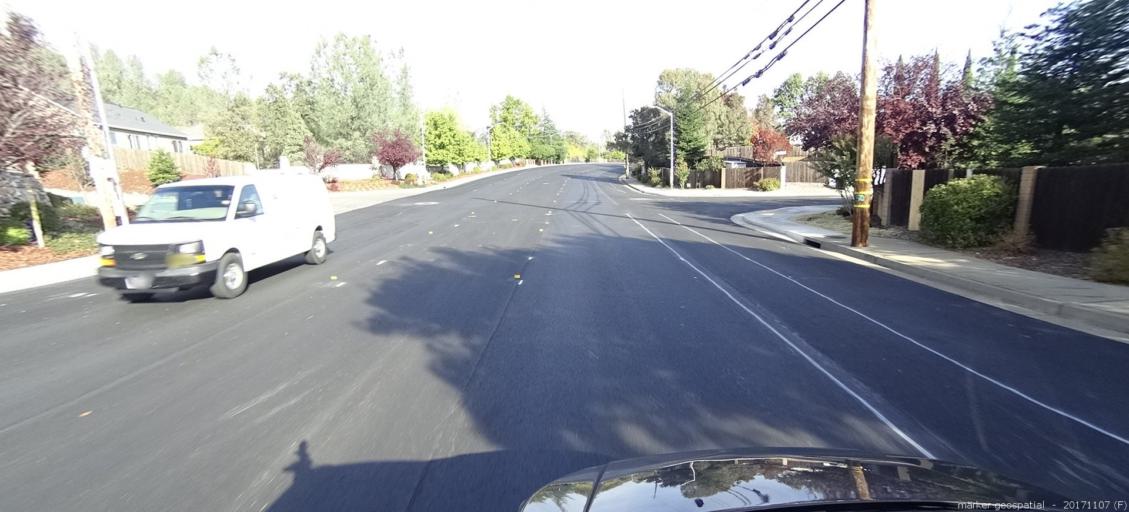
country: US
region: California
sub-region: Shasta County
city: Redding
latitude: 40.5635
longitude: -122.4324
